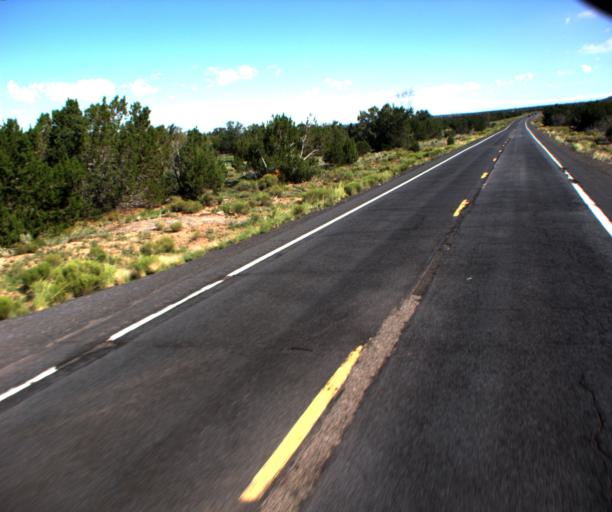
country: US
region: Arizona
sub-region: Coconino County
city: Williams
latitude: 35.4393
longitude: -112.1715
